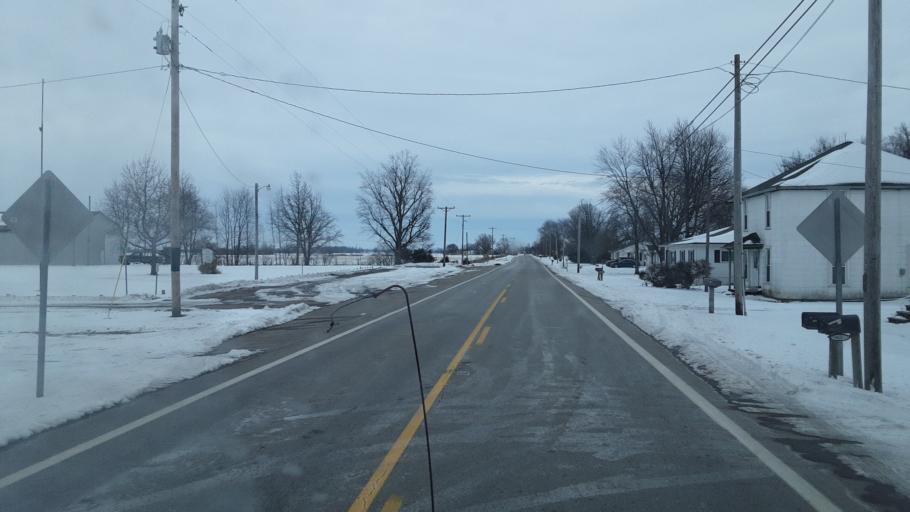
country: US
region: Ohio
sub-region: Madison County
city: Mount Sterling
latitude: 39.6736
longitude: -83.1776
